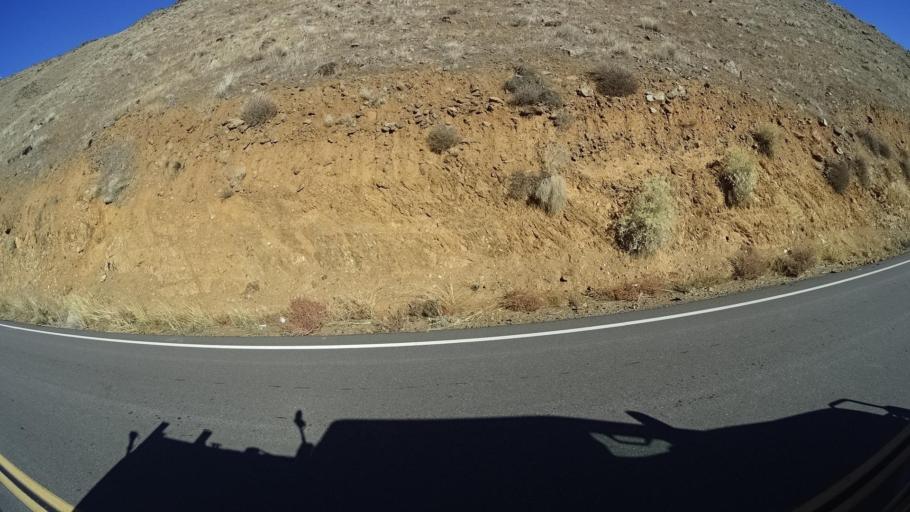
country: US
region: California
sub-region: Kern County
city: Wofford Heights
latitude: 35.6793
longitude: -118.4187
